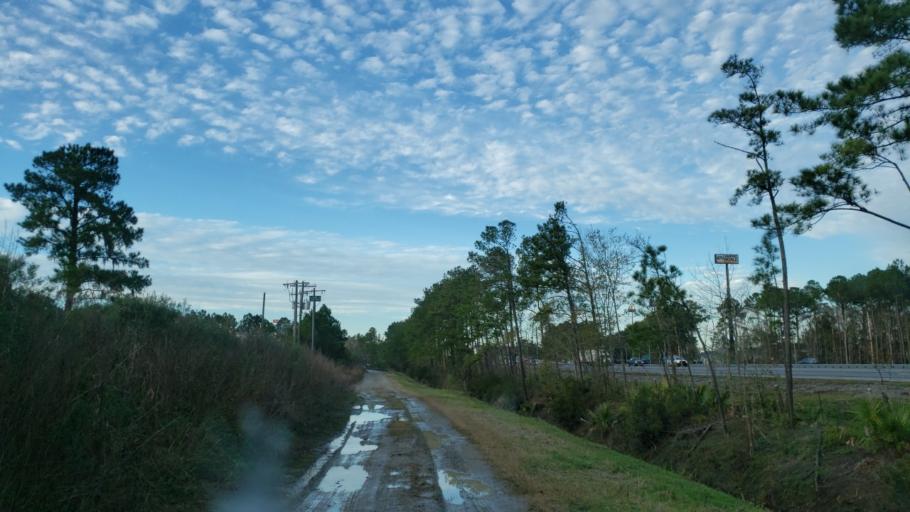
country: US
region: Georgia
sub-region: Chatham County
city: Pooler
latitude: 32.1064
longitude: -81.2381
